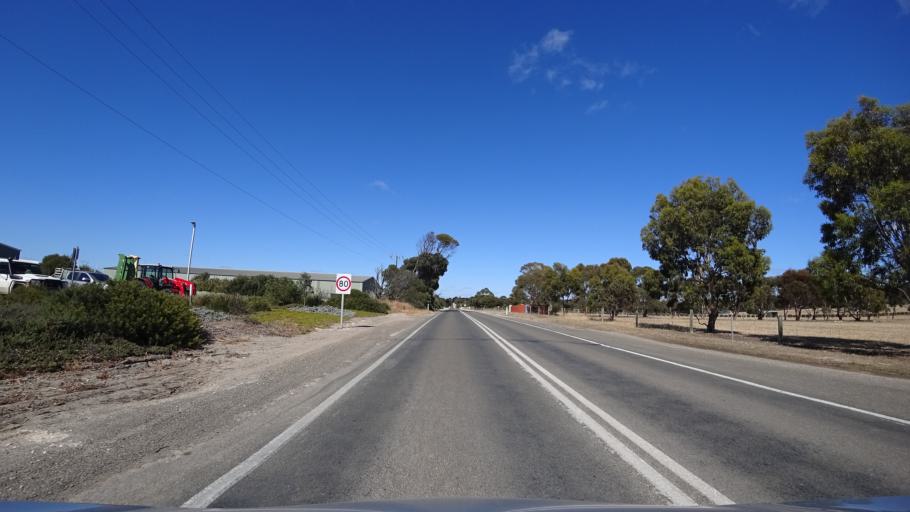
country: AU
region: South Australia
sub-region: Kangaroo Island
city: Kingscote
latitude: -35.6544
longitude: 137.6215
